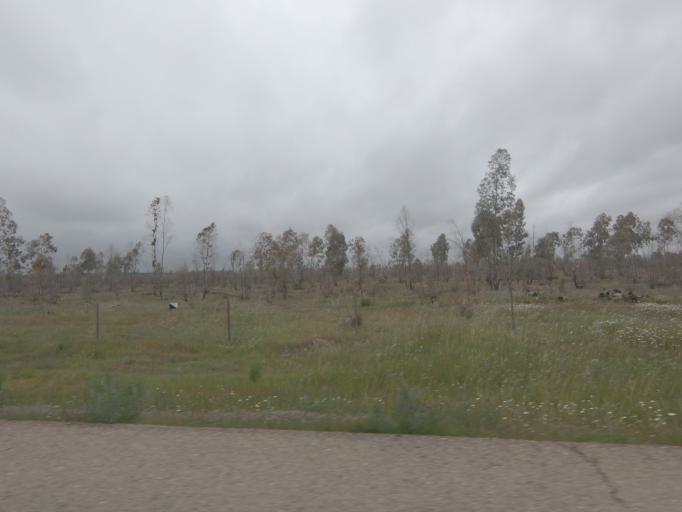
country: ES
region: Extremadura
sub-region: Provincia de Badajoz
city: Badajoz
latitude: 38.9844
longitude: -6.8808
